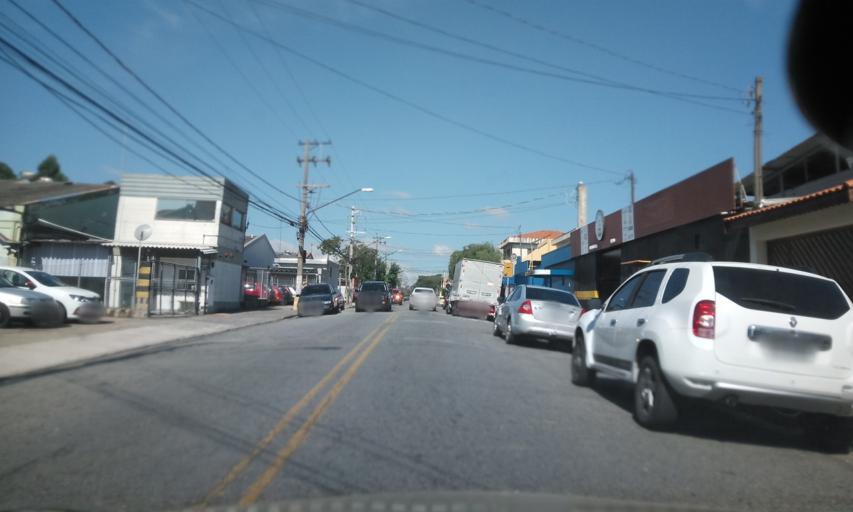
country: BR
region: Sao Paulo
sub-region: Sao Bernardo Do Campo
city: Sao Bernardo do Campo
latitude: -23.7027
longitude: -46.5801
